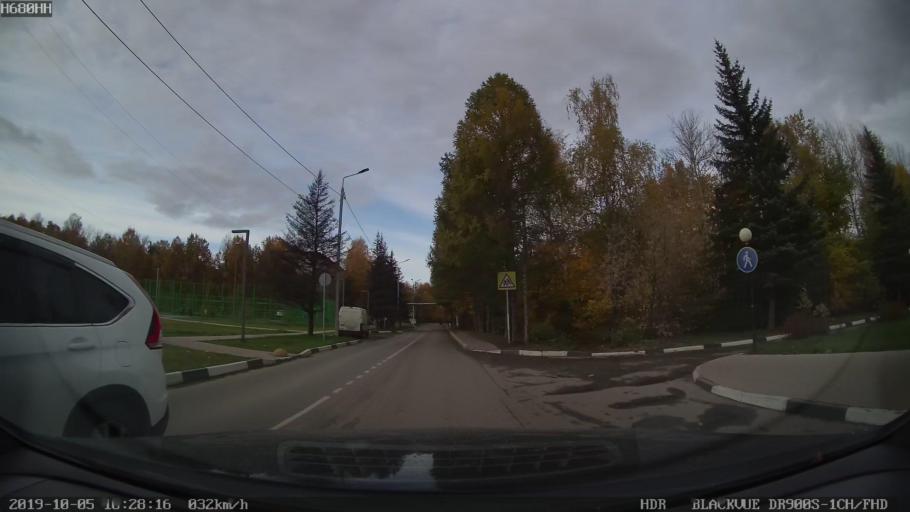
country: RU
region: Moskovskaya
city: Solnechnogorsk
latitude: 56.2157
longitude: 37.0283
